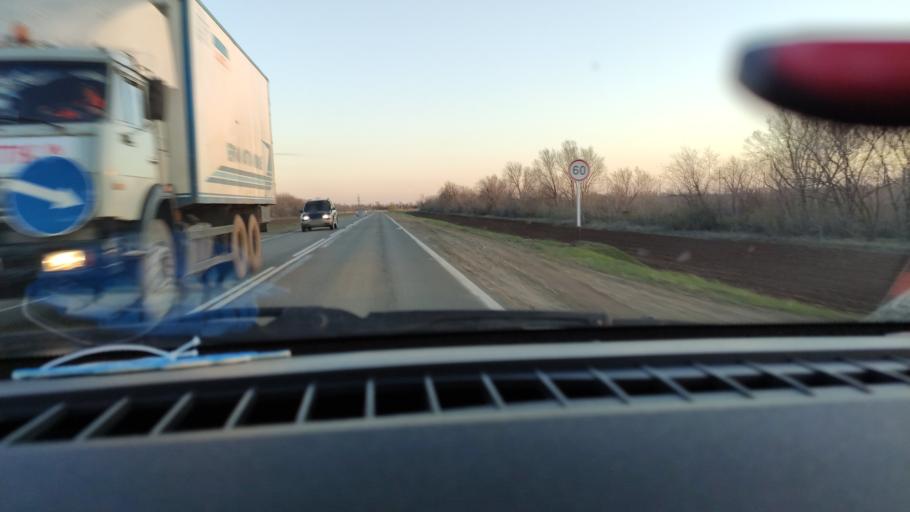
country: RU
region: Saratov
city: Privolzhskiy
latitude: 51.3336
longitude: 46.0385
